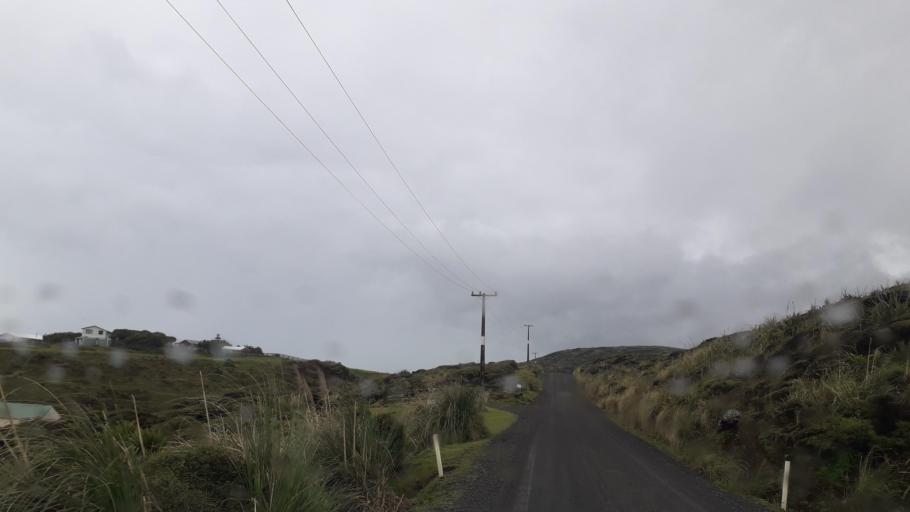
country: NZ
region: Northland
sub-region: Far North District
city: Ahipara
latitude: -35.4330
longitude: 173.2799
